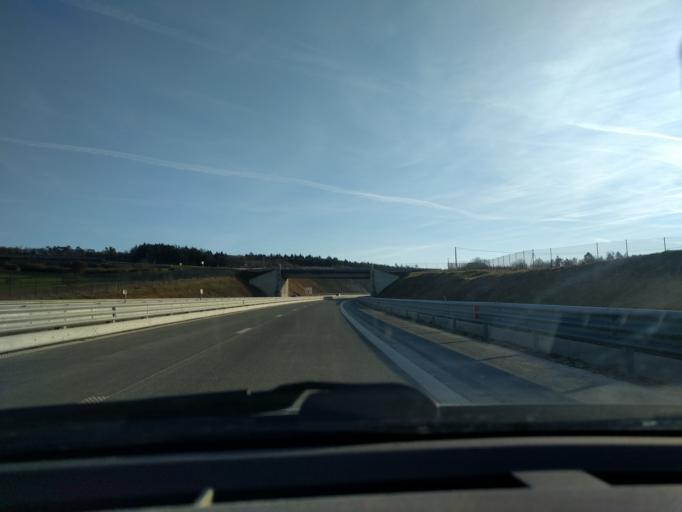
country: BE
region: Wallonia
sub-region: Province de Namur
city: Couvin
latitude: 50.0479
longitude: 4.5121
